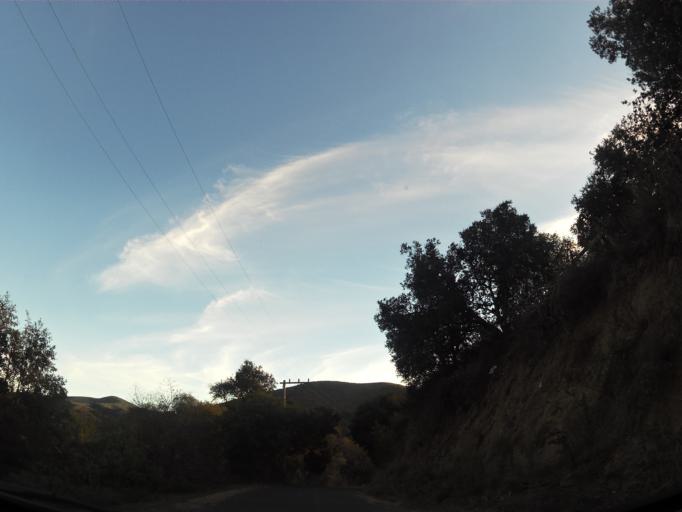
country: US
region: California
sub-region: Monterey County
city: Prunedale
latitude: 36.7793
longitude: -121.5949
